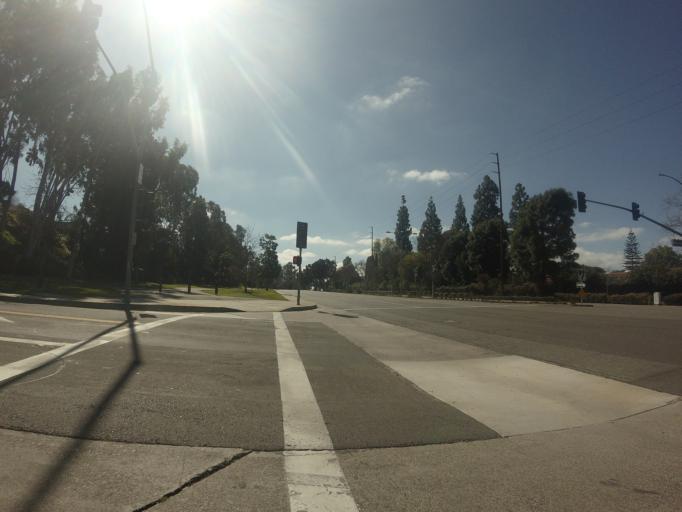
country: US
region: California
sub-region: Orange County
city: Laguna Hills
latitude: 33.6000
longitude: -117.7018
